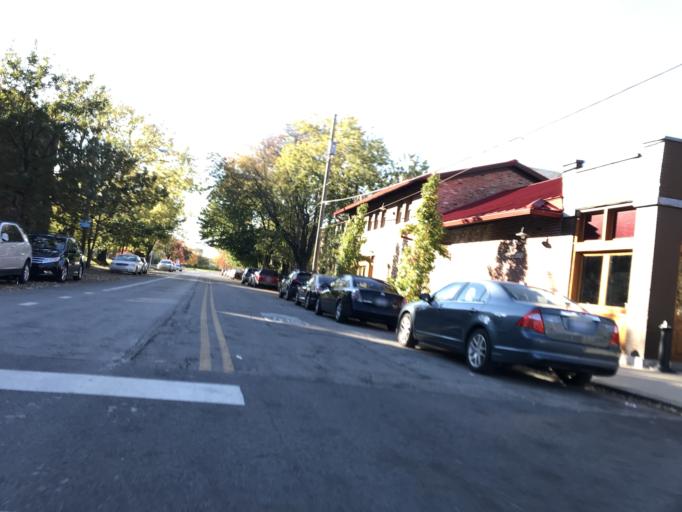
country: US
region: Kentucky
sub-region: Jefferson County
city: Louisville
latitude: 38.2247
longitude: -85.7622
